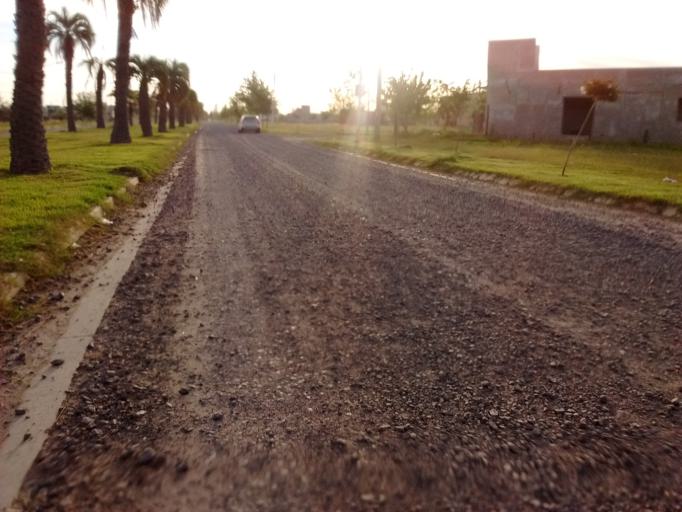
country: AR
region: Santa Fe
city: Roldan
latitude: -32.9371
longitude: -60.8793
